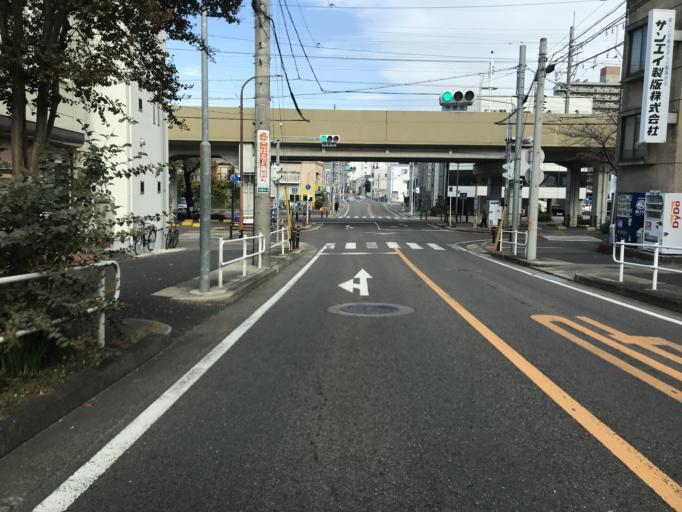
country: JP
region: Aichi
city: Nagoya-shi
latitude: 35.1879
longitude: 136.9242
